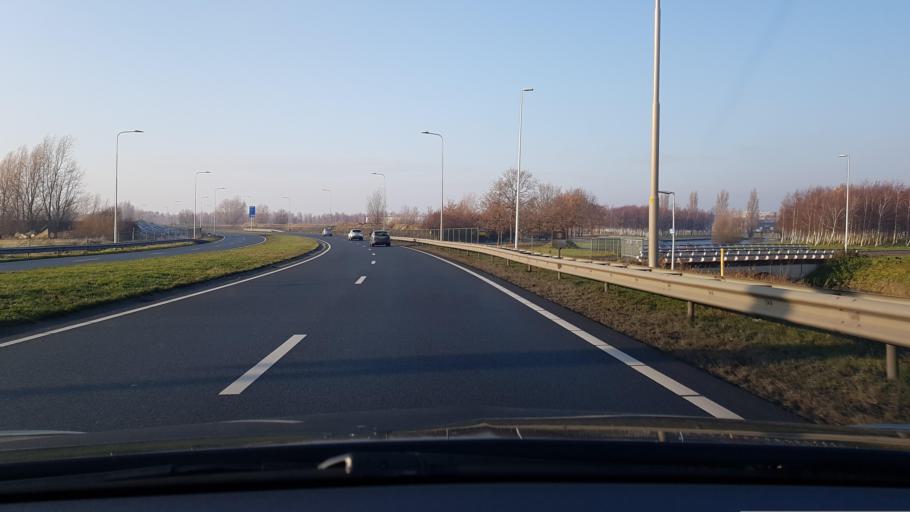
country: NL
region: North Holland
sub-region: Gemeente Aalsmeer
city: Aalsmeer
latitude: 52.2884
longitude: 4.7675
